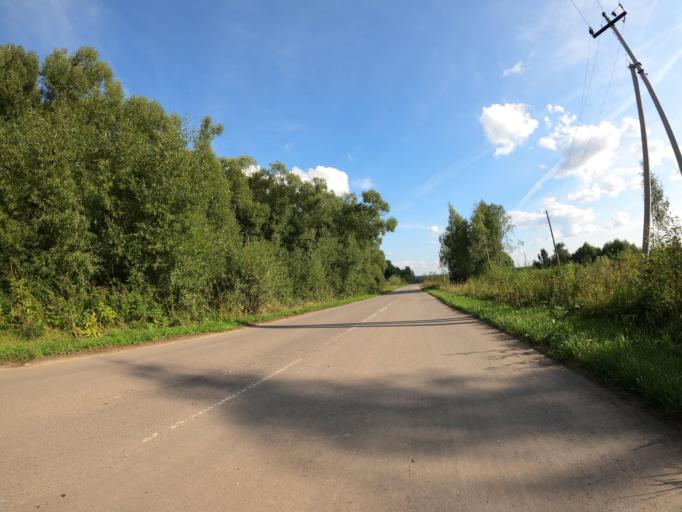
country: RU
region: Moskovskaya
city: Troitskoye
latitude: 55.2090
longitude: 38.4879
